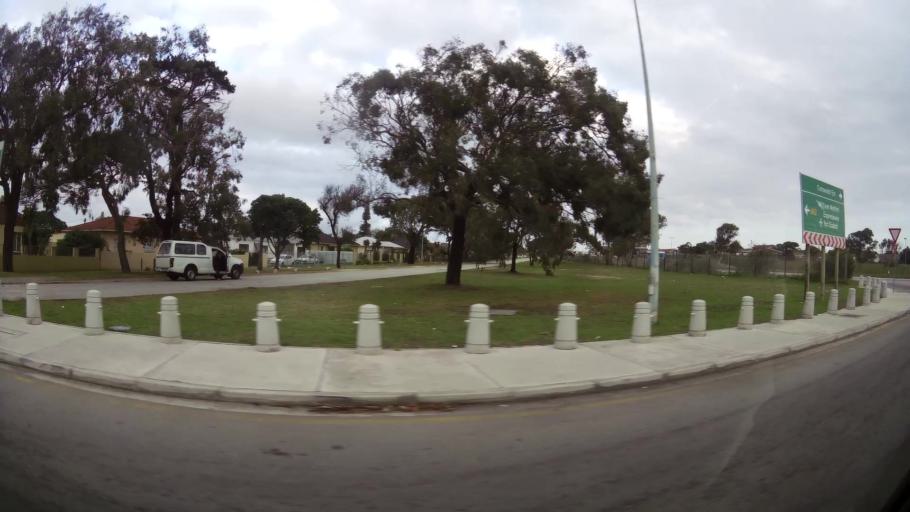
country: ZA
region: Eastern Cape
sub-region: Nelson Mandela Bay Metropolitan Municipality
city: Port Elizabeth
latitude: -33.9408
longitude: 25.5511
